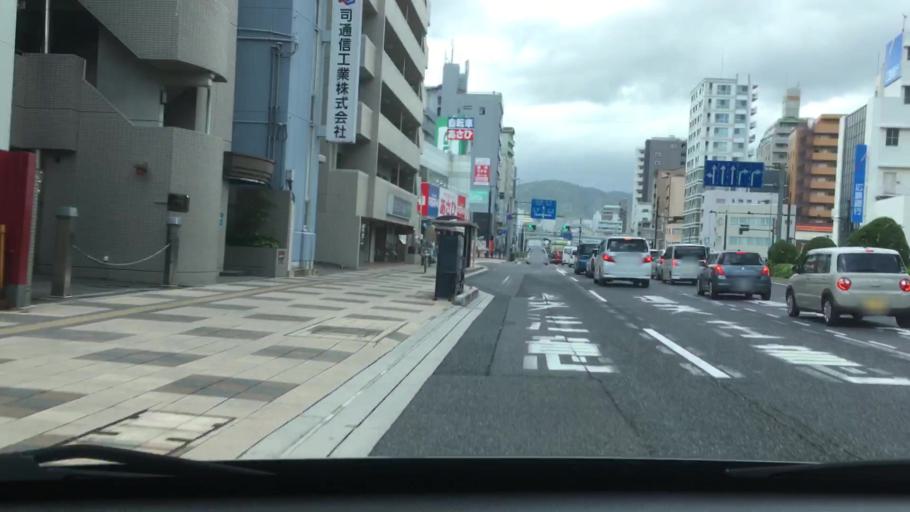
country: JP
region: Hiroshima
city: Hiroshima-shi
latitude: 34.3857
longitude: 132.4444
